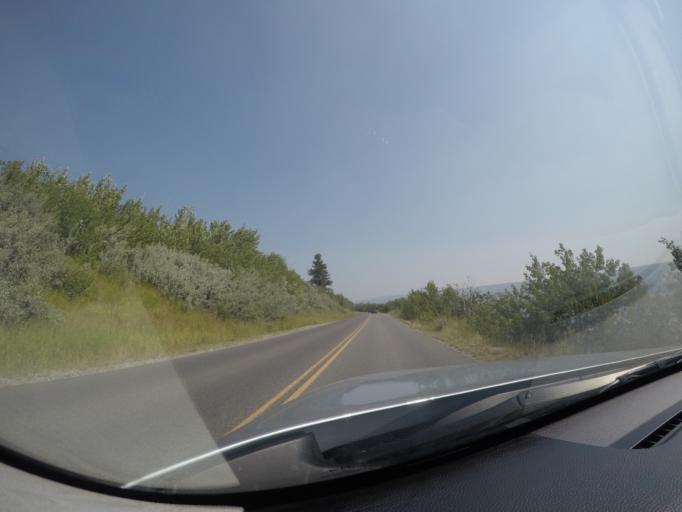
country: US
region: Montana
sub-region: Glacier County
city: North Browning
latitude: 48.7427
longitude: -113.4541
